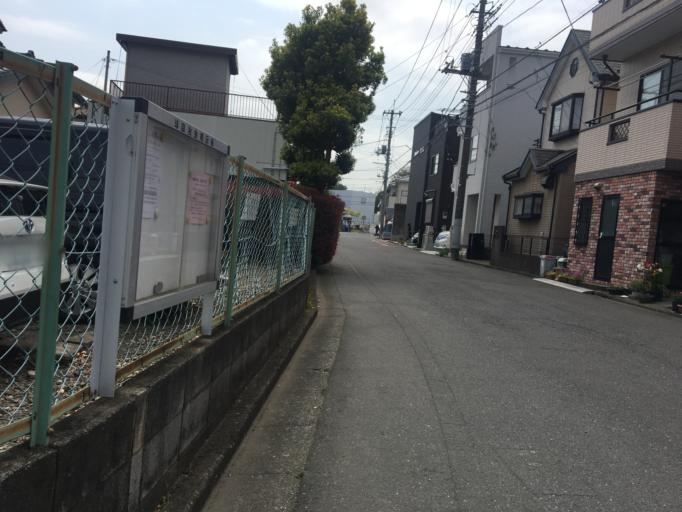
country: JP
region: Saitama
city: Kamifukuoka
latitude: 35.8848
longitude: 139.5220
